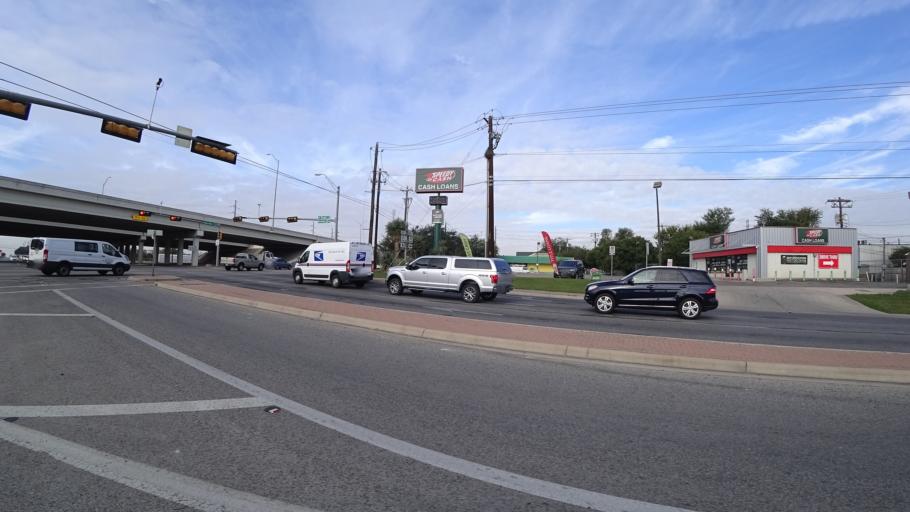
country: US
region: Texas
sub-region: Travis County
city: Austin
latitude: 30.2158
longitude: -97.7346
